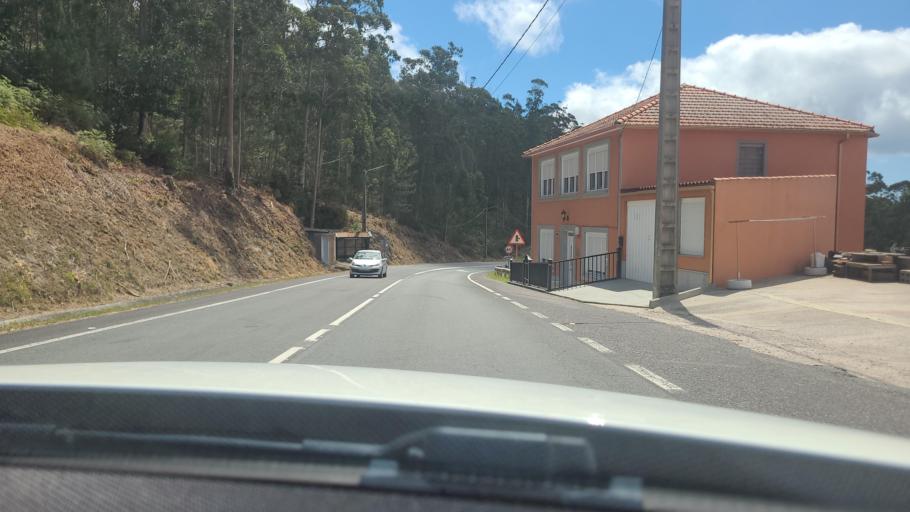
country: ES
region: Galicia
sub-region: Provincia da Coruna
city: Corcubion
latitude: 42.9162
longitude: -9.1460
